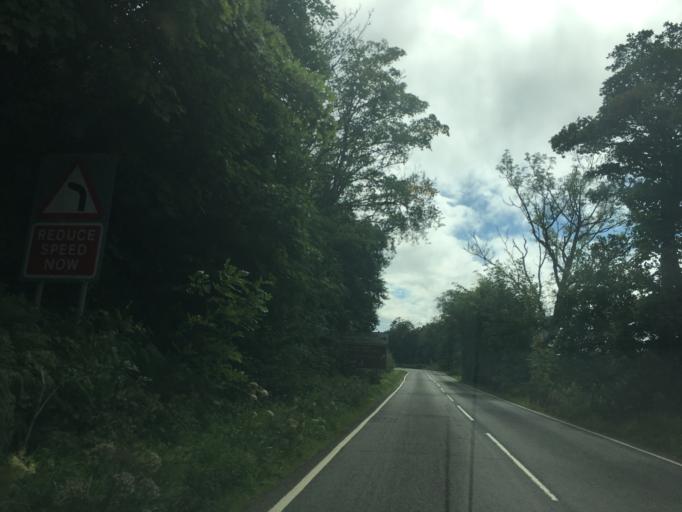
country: GB
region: Scotland
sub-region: Argyll and Bute
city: Lochgilphead
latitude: 56.1235
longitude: -5.4907
